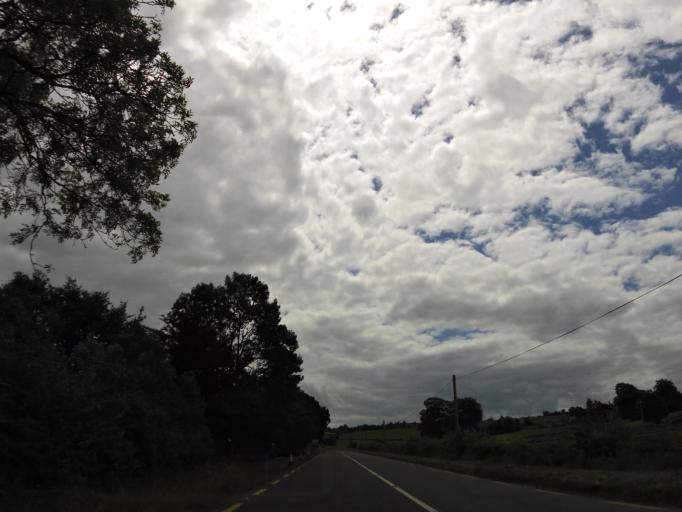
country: IE
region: Munster
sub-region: North Tipperary
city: Nenagh
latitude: 52.7753
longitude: -8.0287
